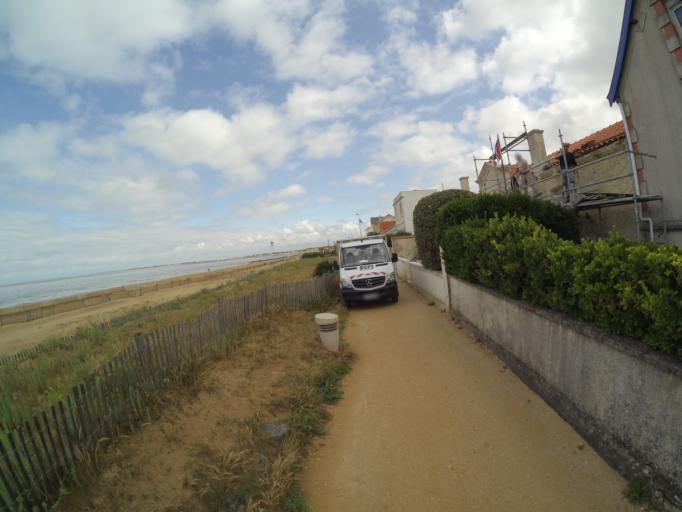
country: FR
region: Poitou-Charentes
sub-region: Departement de la Charente-Maritime
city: Chatelaillon-Plage
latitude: 46.0691
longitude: -1.0928
